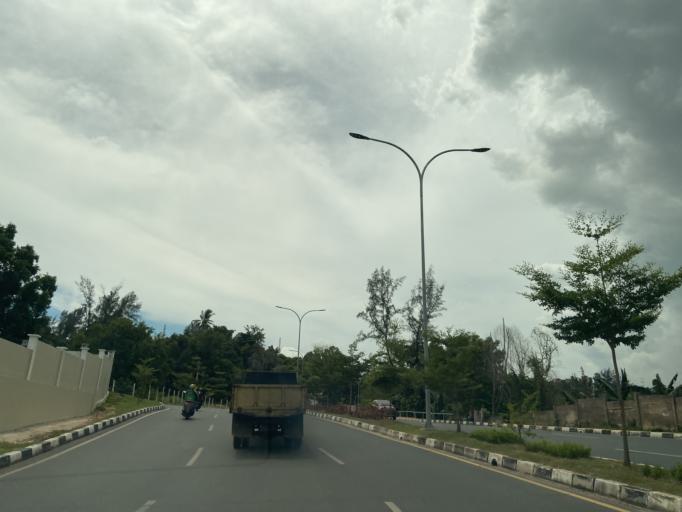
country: SG
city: Singapore
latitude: 1.1517
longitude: 104.0082
